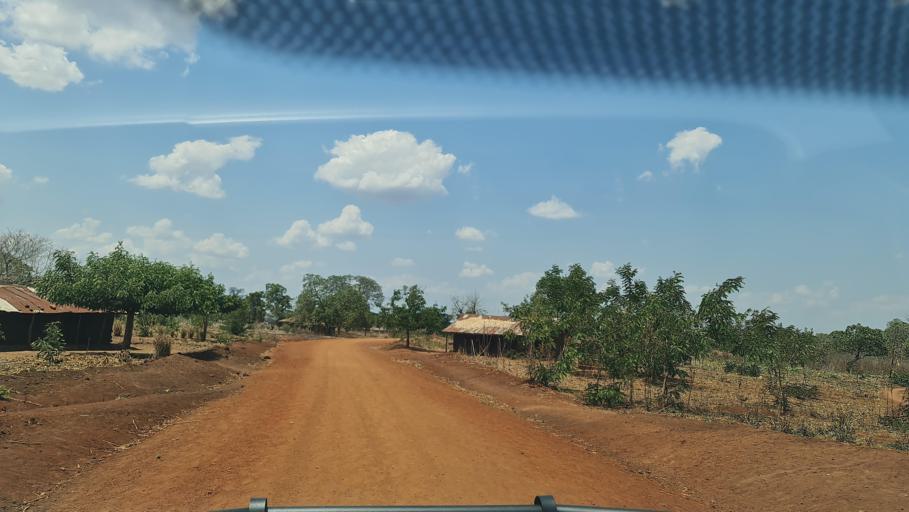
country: MZ
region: Nampula
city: Nacala
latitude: -14.8081
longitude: 40.0726
